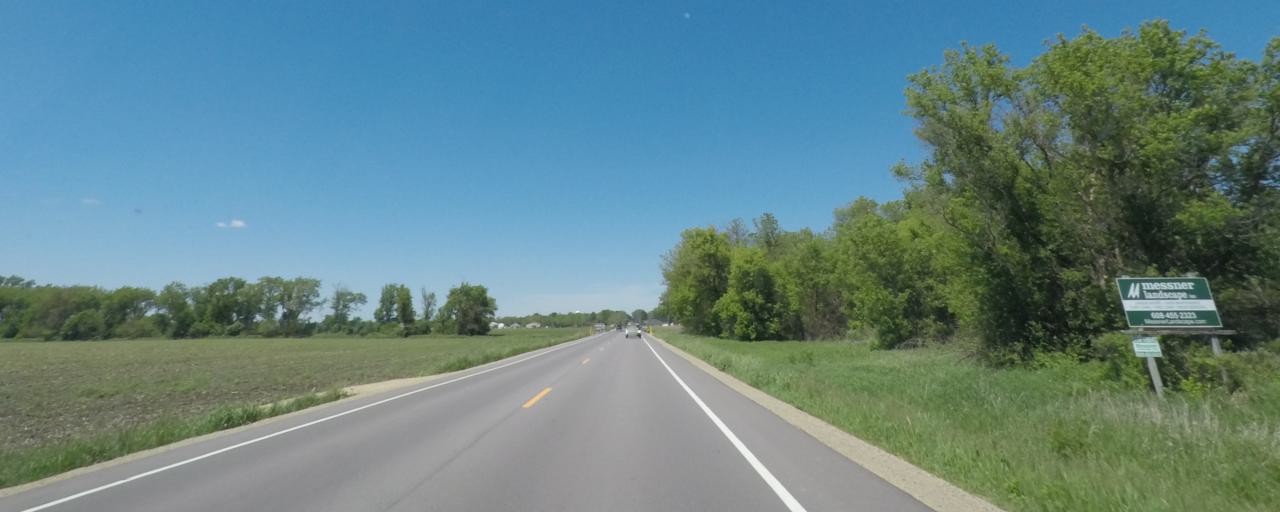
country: US
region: Wisconsin
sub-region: Green County
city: Brooklyn
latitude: 42.8386
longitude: -89.3692
